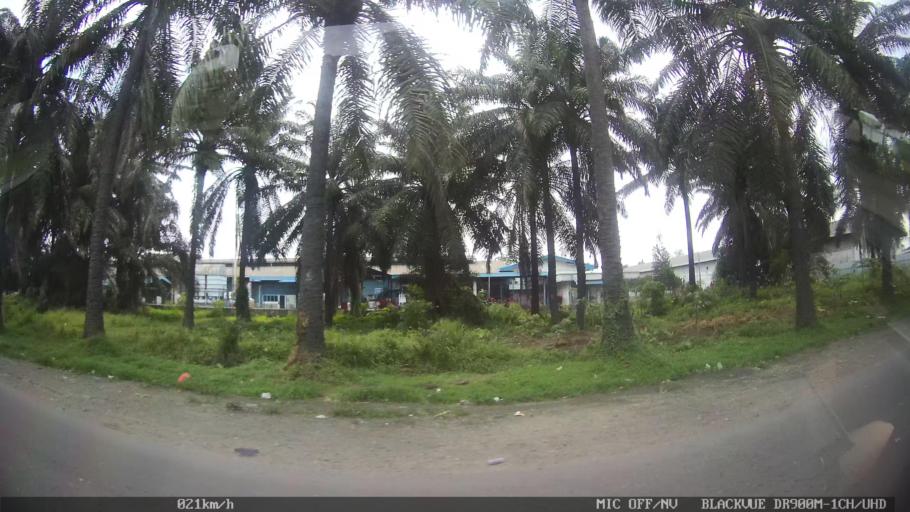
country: ID
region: North Sumatra
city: Labuhan Deli
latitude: 3.6732
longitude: 98.6786
